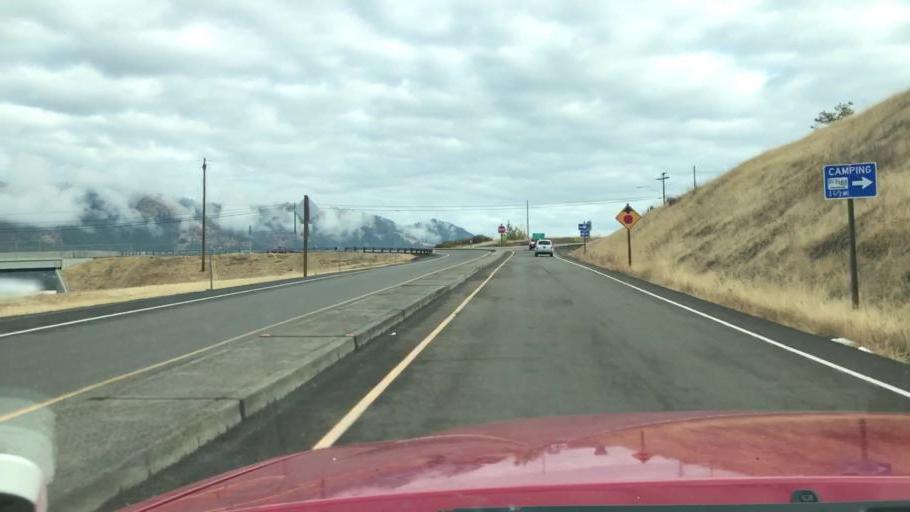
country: US
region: Oregon
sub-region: Douglas County
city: Tri-City
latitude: 42.9721
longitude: -123.3356
